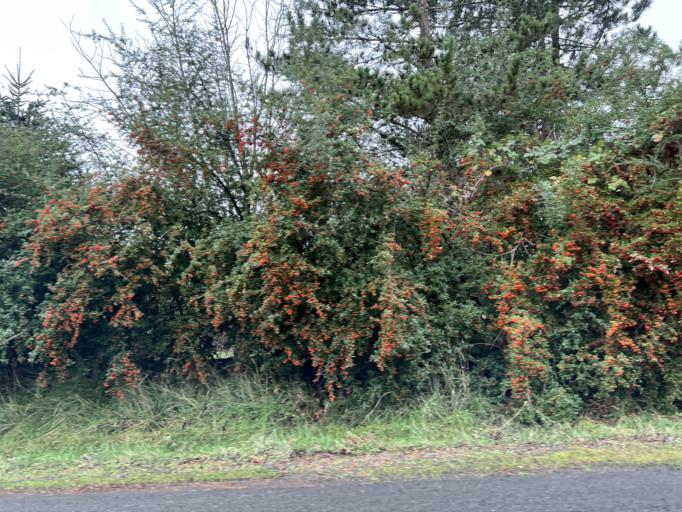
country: US
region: Oregon
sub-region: Polk County
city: Independence
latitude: 44.8120
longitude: -123.0872
